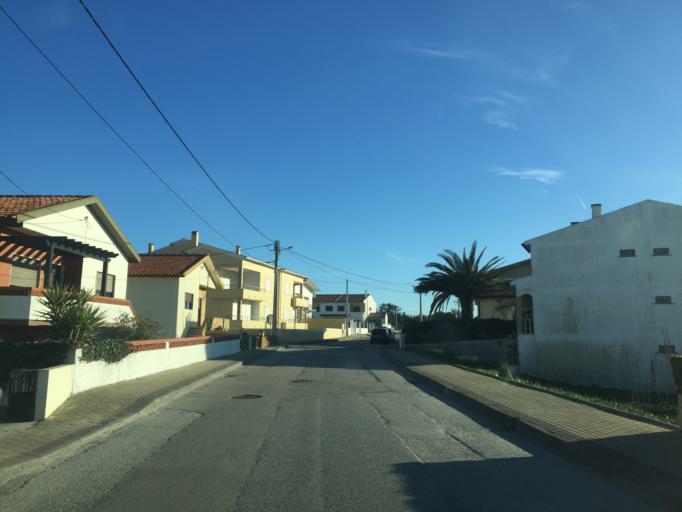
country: PT
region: Coimbra
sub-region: Figueira da Foz
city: Lavos
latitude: 40.0892
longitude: -8.8732
